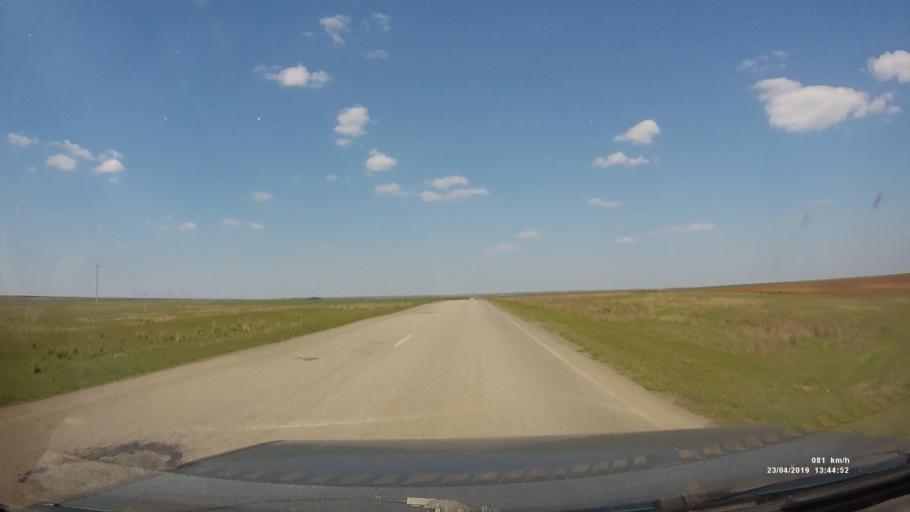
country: RU
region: Kalmykiya
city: Yashalta
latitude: 46.5858
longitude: 42.8187
